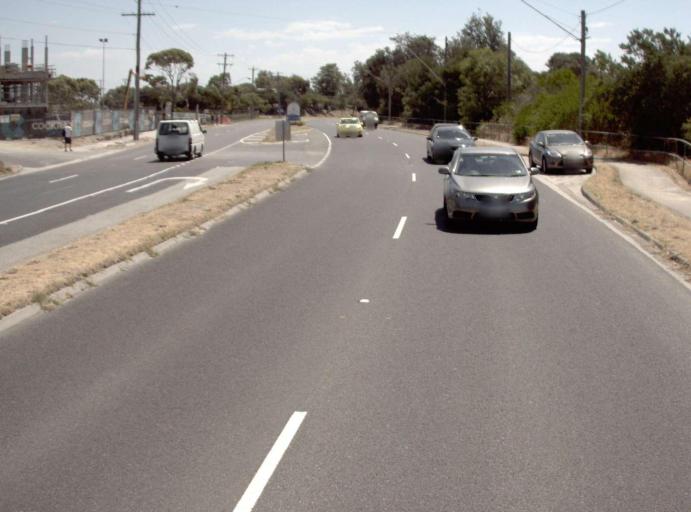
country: AU
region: Victoria
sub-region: Frankston
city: Frankston
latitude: -38.1497
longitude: 145.1292
